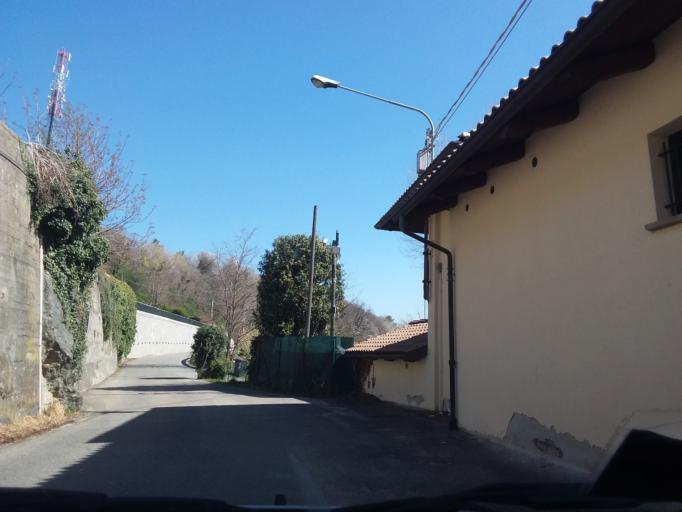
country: IT
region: Piedmont
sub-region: Provincia di Torino
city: Rosta
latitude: 45.0633
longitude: 7.4922
